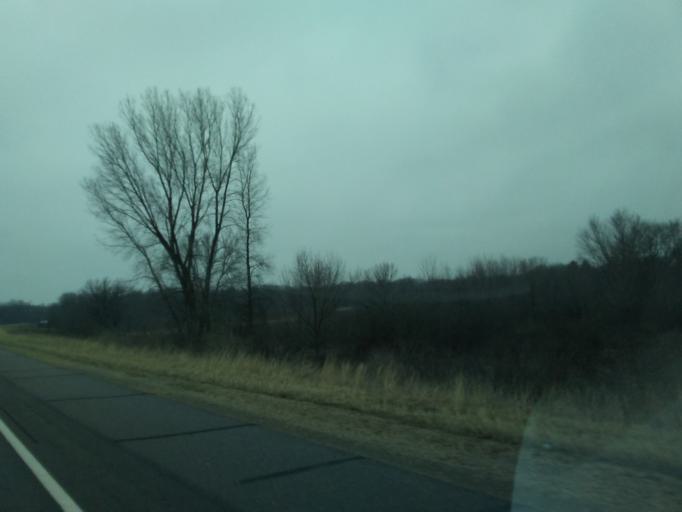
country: US
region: Wisconsin
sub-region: Sauk County
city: Spring Green
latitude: 43.1630
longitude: -90.0315
